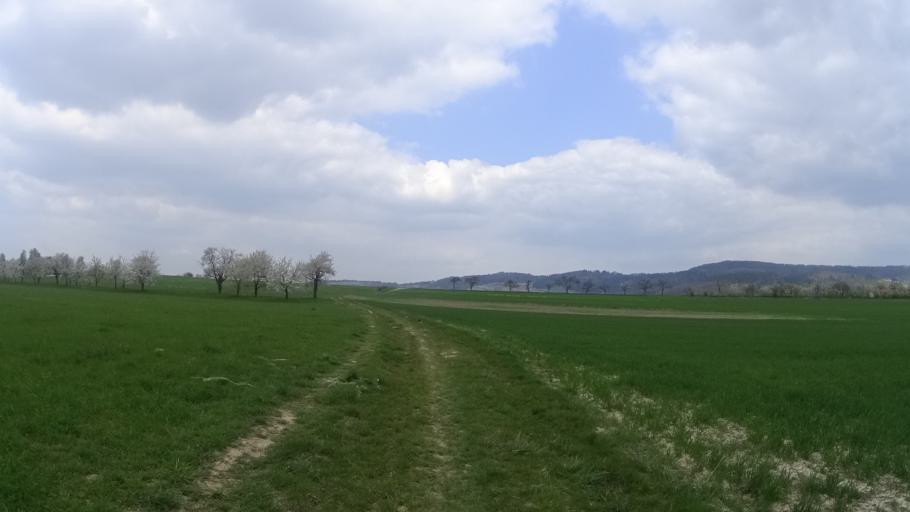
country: DE
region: Bavaria
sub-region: Upper Franconia
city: Kleinsendelbach
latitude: 49.6045
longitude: 11.1790
